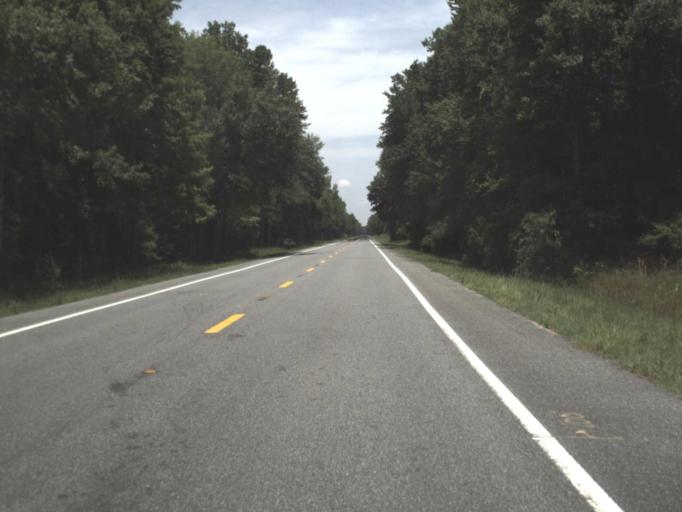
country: US
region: Florida
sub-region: Lafayette County
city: Mayo
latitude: 29.8936
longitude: -83.2991
